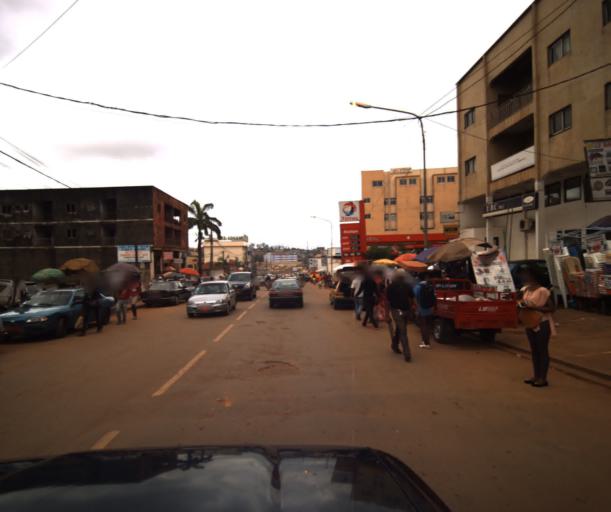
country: CM
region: Centre
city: Yaounde
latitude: 3.8495
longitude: 11.5213
